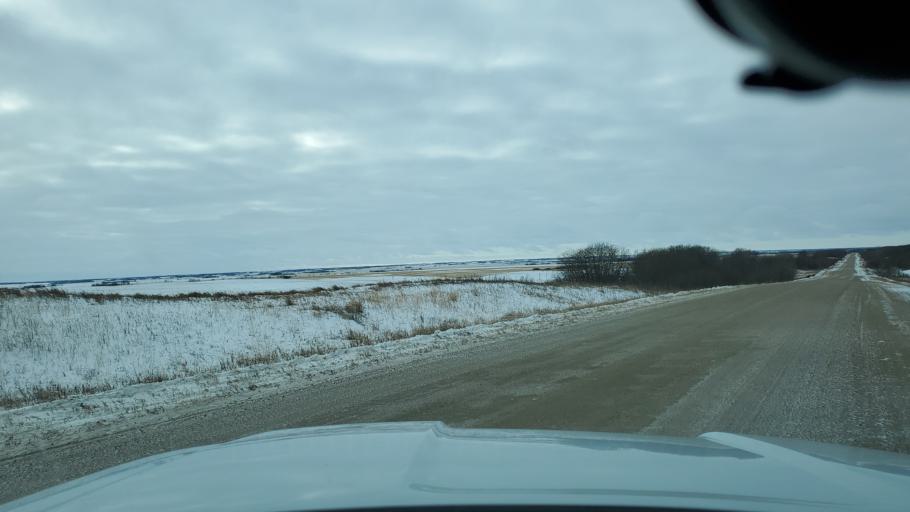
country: CA
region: Saskatchewan
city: White City
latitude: 50.7468
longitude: -104.1606
